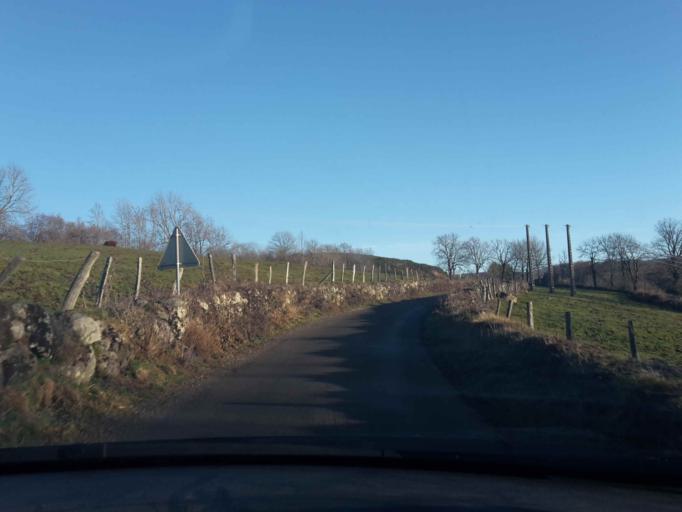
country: FR
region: Auvergne
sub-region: Departement du Cantal
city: Ydes
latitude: 45.2391
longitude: 2.5442
